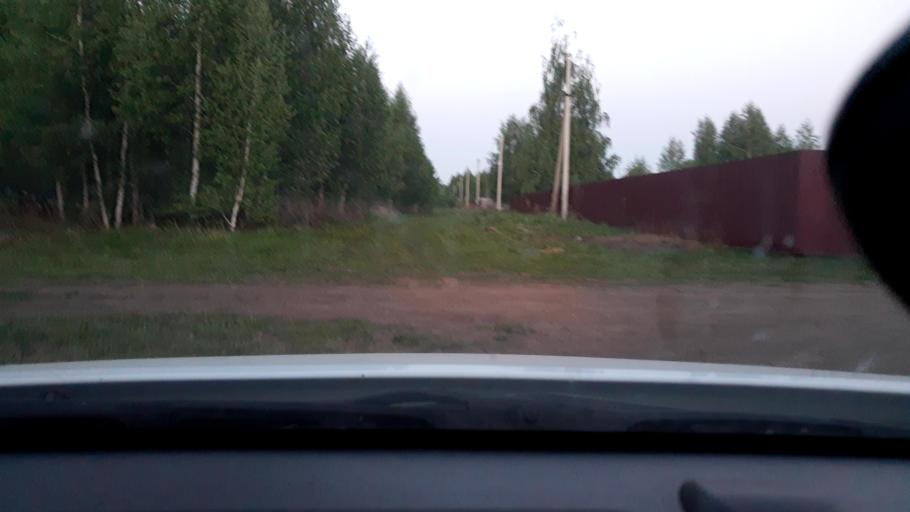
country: RU
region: Bashkortostan
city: Avdon
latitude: 54.5342
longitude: 55.8168
